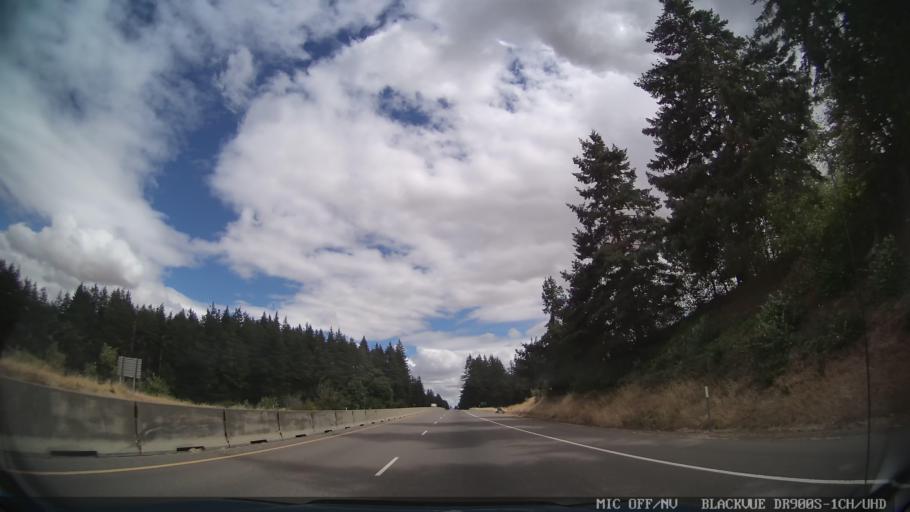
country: US
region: Oregon
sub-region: Marion County
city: Four Corners
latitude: 44.8973
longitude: -122.9373
